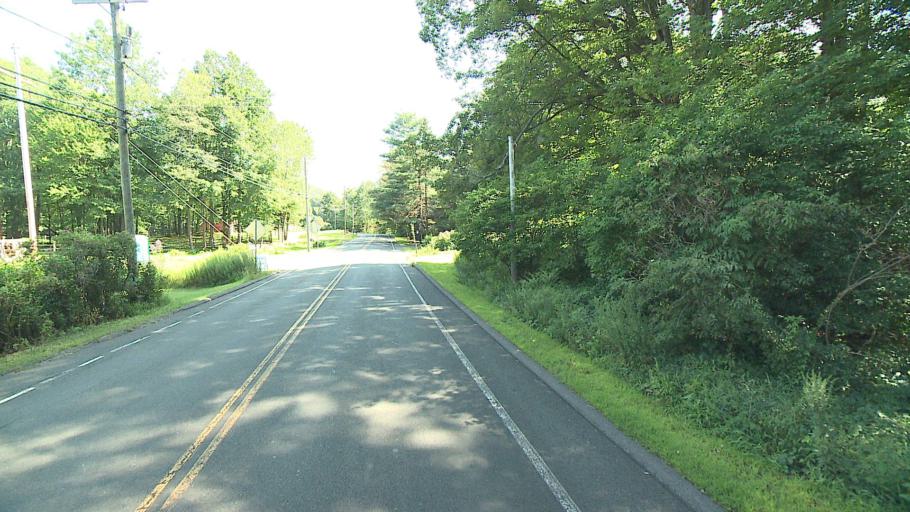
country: US
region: Connecticut
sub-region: Hartford County
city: West Simsbury
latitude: 41.8827
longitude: -72.8708
